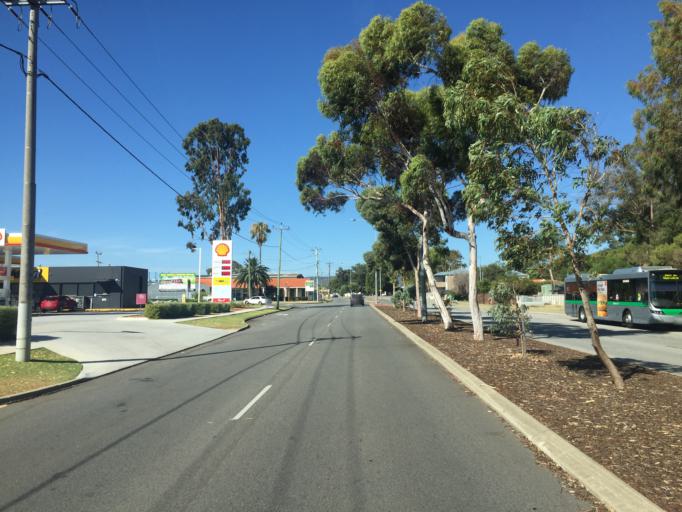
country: AU
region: Western Australia
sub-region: Gosnells
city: Maddington
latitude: -32.0459
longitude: 115.9886
